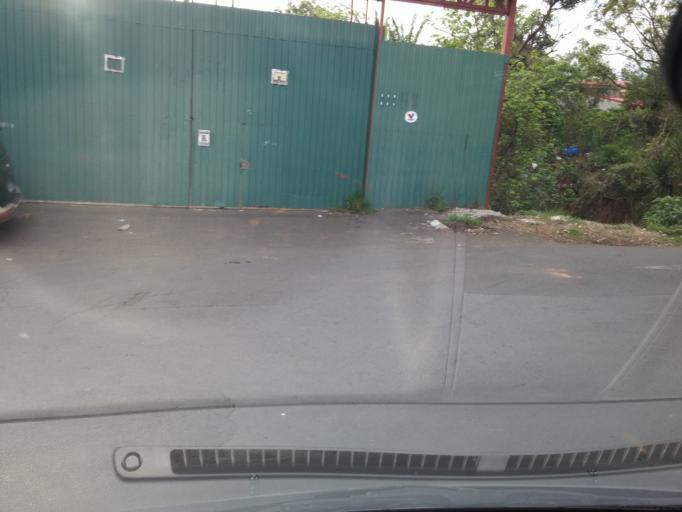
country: CR
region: Heredia
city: San Rafael
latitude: 10.0138
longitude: -84.1107
